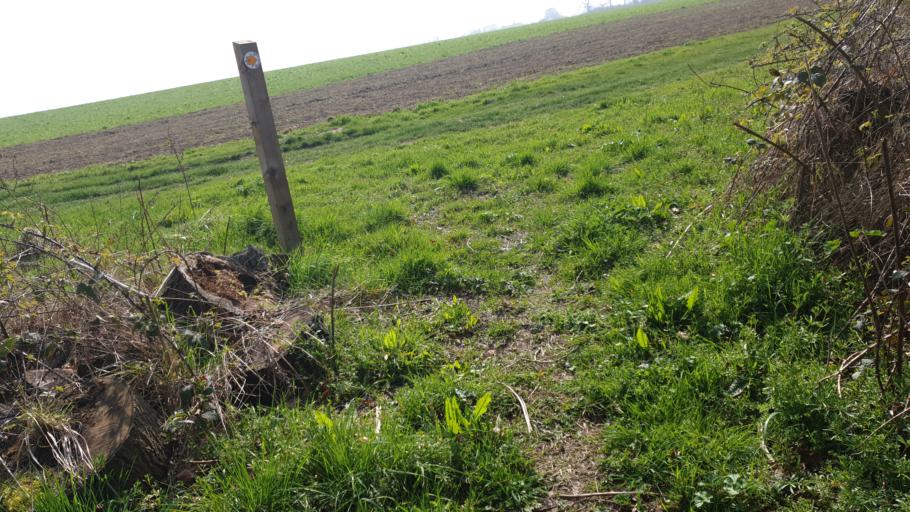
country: GB
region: England
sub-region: Essex
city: Mistley
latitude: 51.9287
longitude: 1.1622
